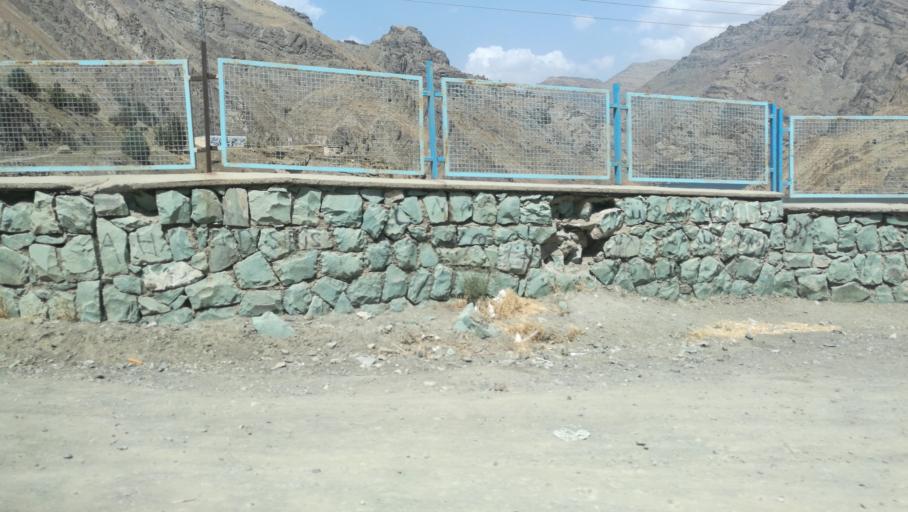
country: IR
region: Alborz
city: Karaj
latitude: 35.9775
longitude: 51.0942
